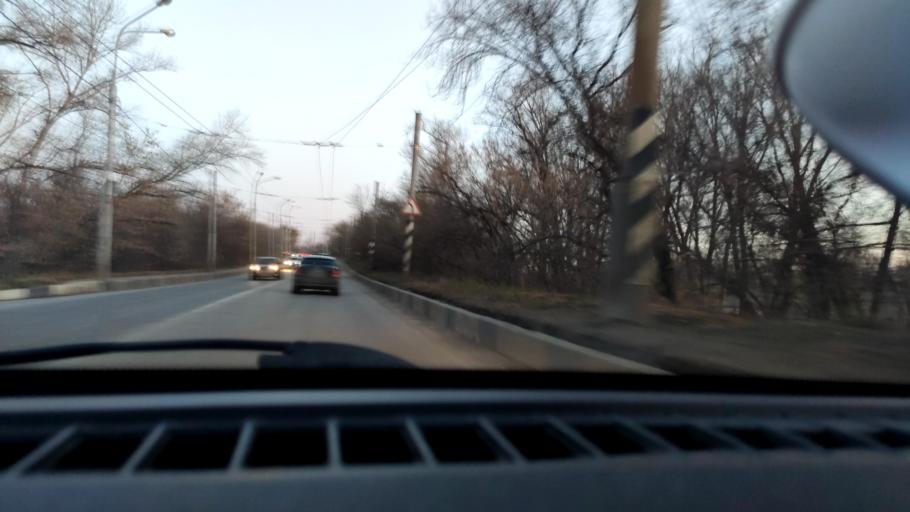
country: RU
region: Samara
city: Samara
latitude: 53.1489
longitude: 50.0945
